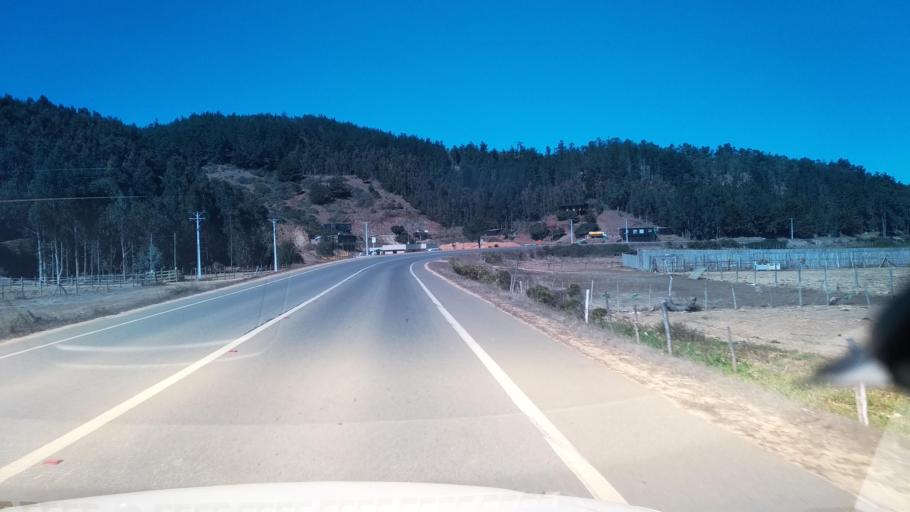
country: CL
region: O'Higgins
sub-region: Provincia de Colchagua
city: Santa Cruz
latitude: -34.4665
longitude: -72.0206
